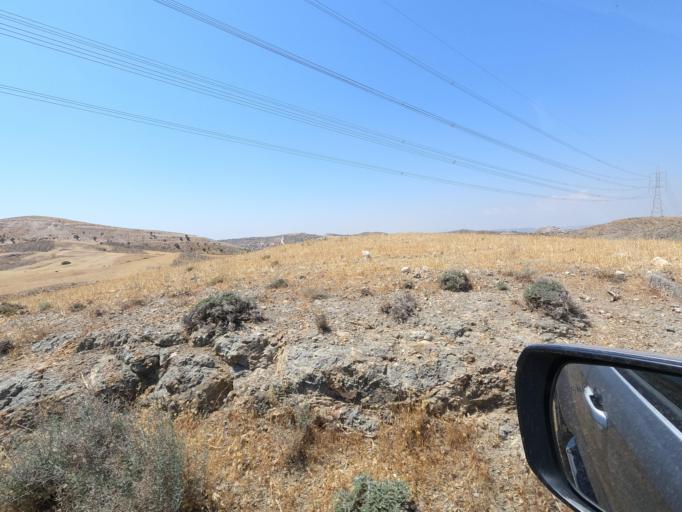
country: CY
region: Larnaka
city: Troulloi
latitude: 35.0005
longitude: 33.6150
